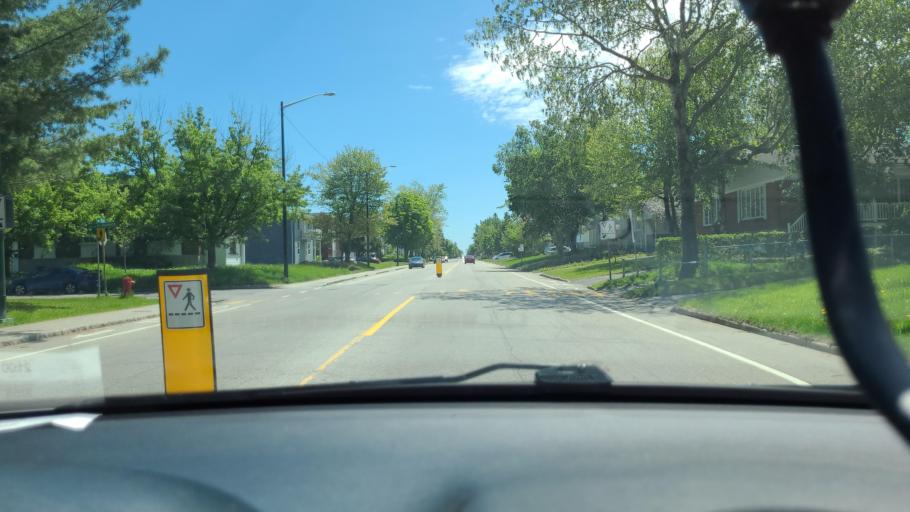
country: CA
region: Quebec
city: L'Ancienne-Lorette
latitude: 46.7641
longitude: -71.3257
